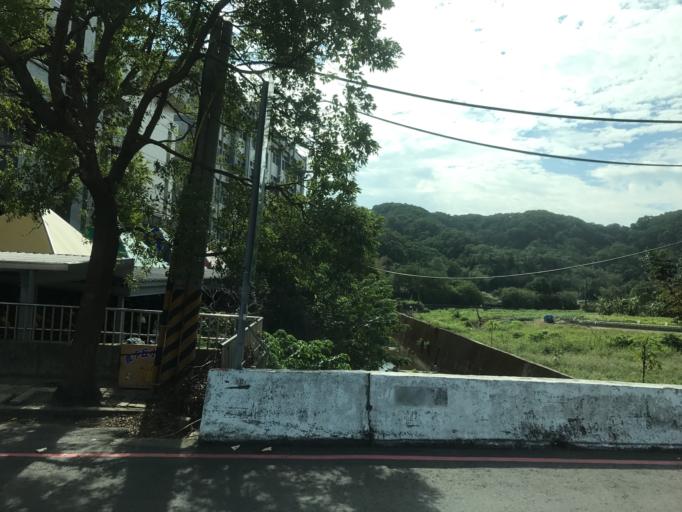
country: TW
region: Taiwan
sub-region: Hsinchu
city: Hsinchu
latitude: 24.7782
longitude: 120.9399
